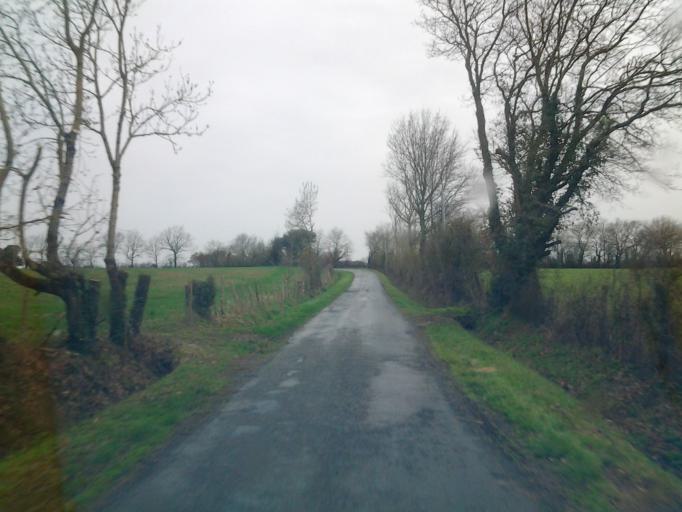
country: FR
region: Pays de la Loire
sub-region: Departement de la Vendee
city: Nesmy
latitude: 46.6319
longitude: -1.3752
